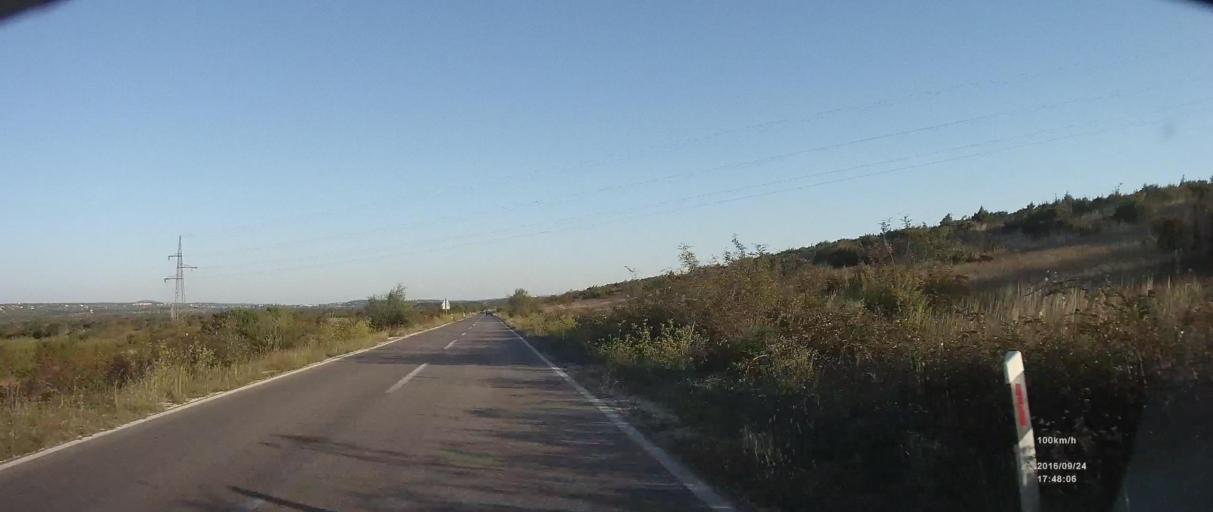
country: HR
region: Zadarska
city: Polaca
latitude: 44.0673
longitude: 15.5332
